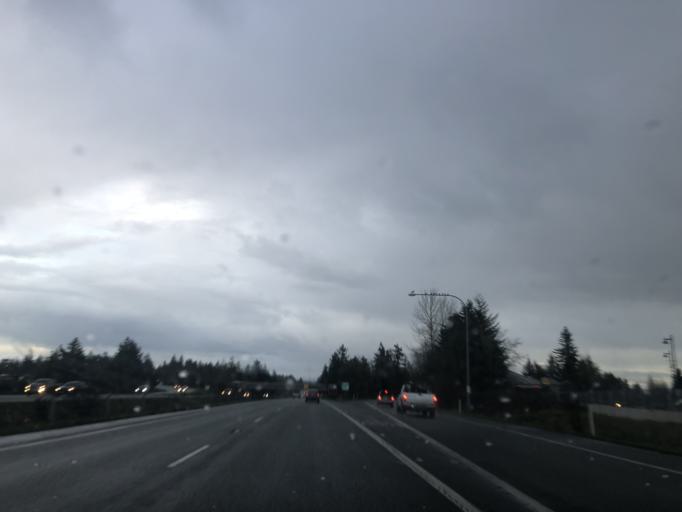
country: US
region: Washington
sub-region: Pierce County
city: Gig Harbor
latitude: 47.3083
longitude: -122.5793
